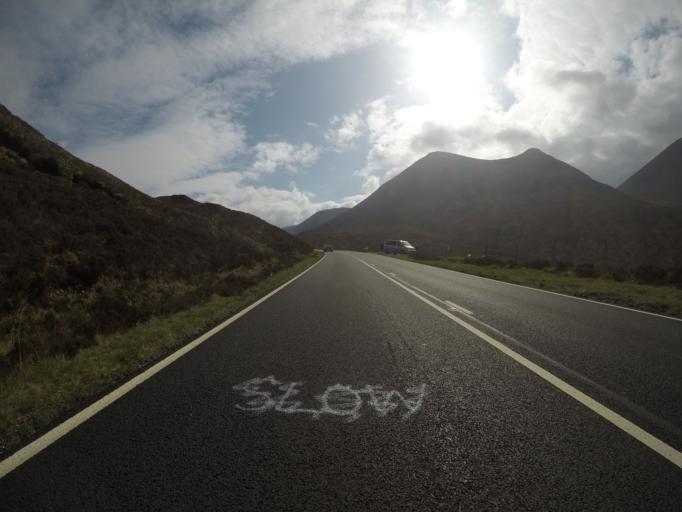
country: GB
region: Scotland
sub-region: Highland
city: Portree
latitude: 57.2886
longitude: -6.0927
